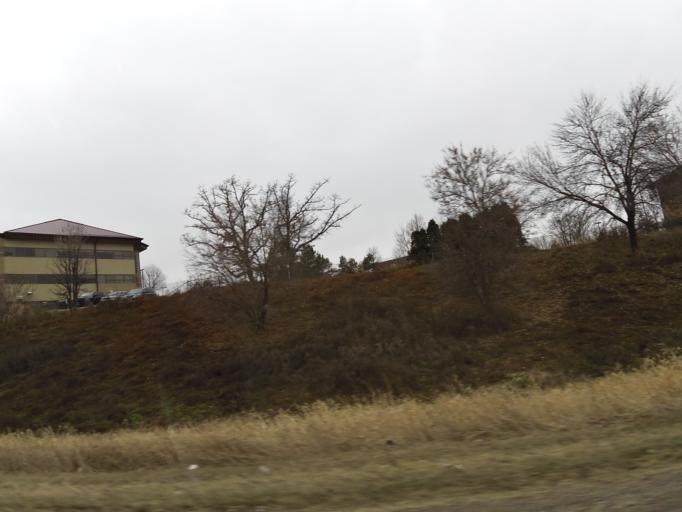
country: US
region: Minnesota
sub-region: Dakota County
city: Burnsville
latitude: 44.7508
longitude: -93.2661
